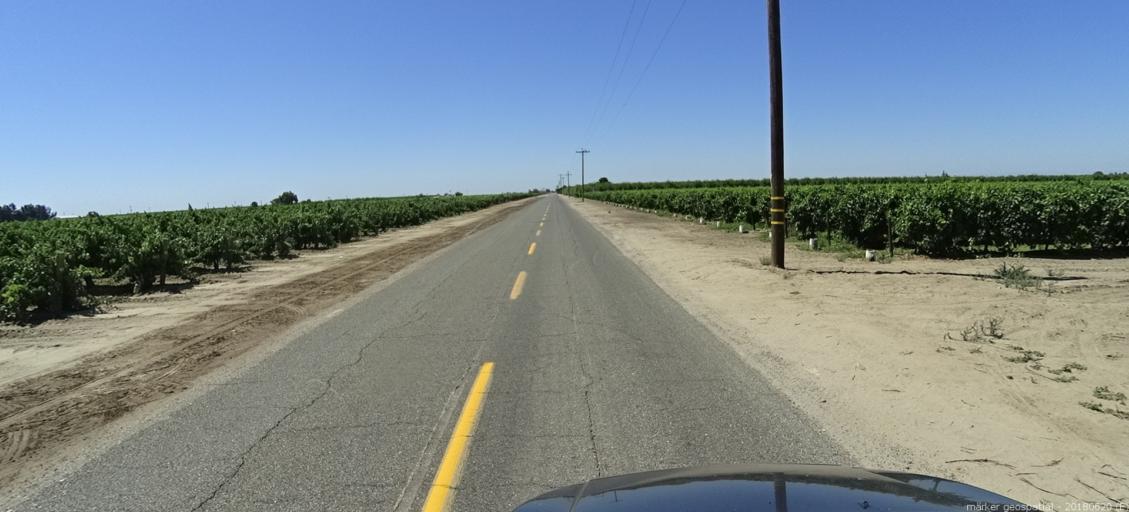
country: US
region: California
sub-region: Fresno County
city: Biola
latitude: 36.8576
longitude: -120.0012
